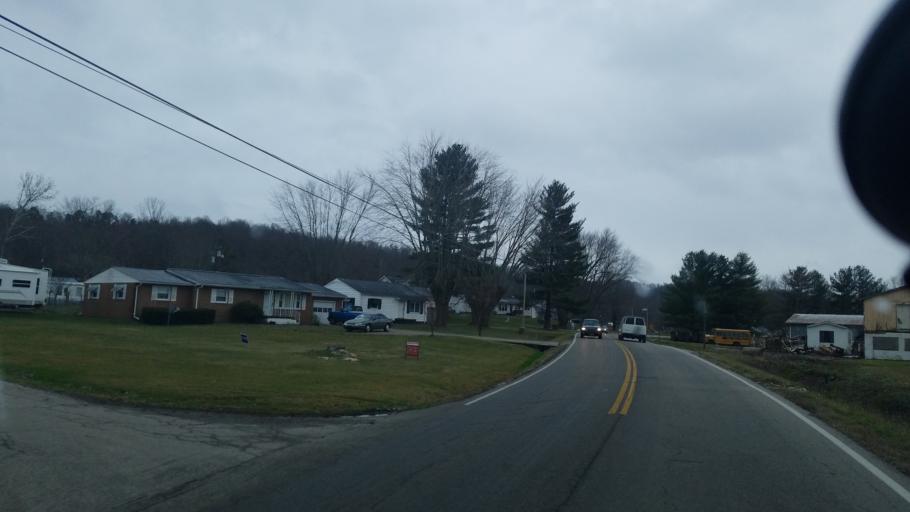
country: US
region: Ohio
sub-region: Scioto County
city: West Portsmouth
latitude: 38.6280
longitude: -83.1277
